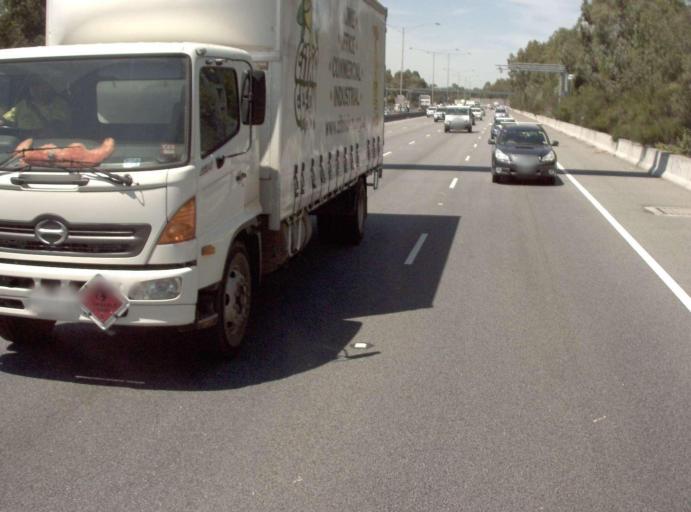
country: AU
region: Victoria
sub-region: Stonnington
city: Glen Iris
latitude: -37.8617
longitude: 145.0597
